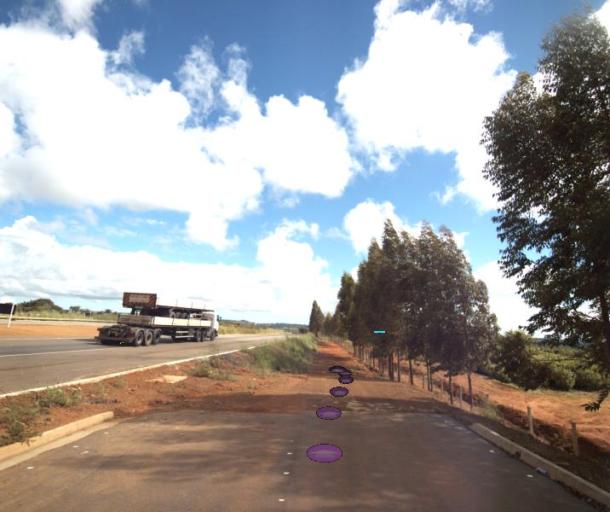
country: BR
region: Goias
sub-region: Anapolis
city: Anapolis
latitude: -16.2301
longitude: -49.0087
